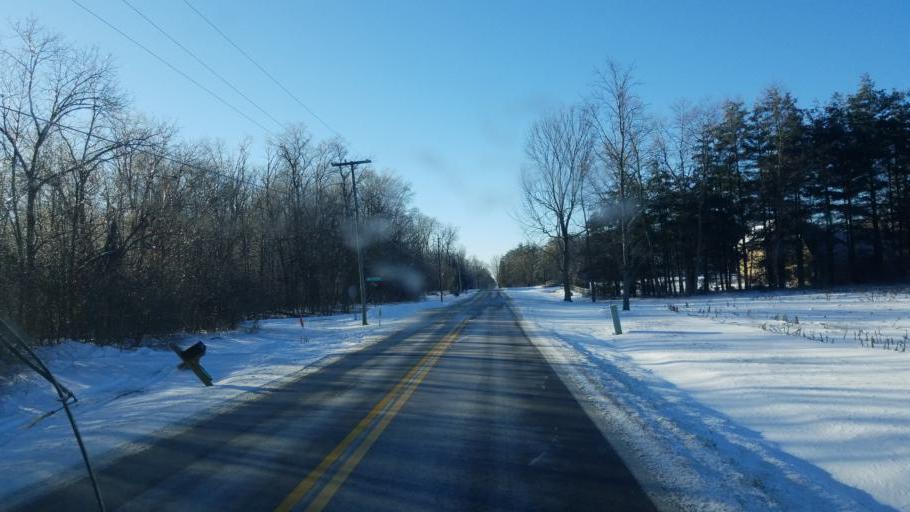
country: US
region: Ohio
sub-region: Delaware County
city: Sunbury
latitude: 40.2391
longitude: -82.9111
